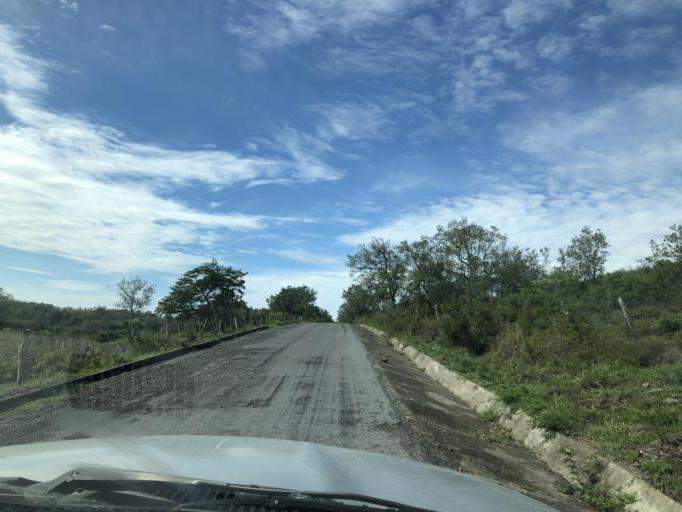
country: MX
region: Veracruz
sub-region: Juchique de Ferrer
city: Plan de las Hayas
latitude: 19.7804
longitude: -96.5564
